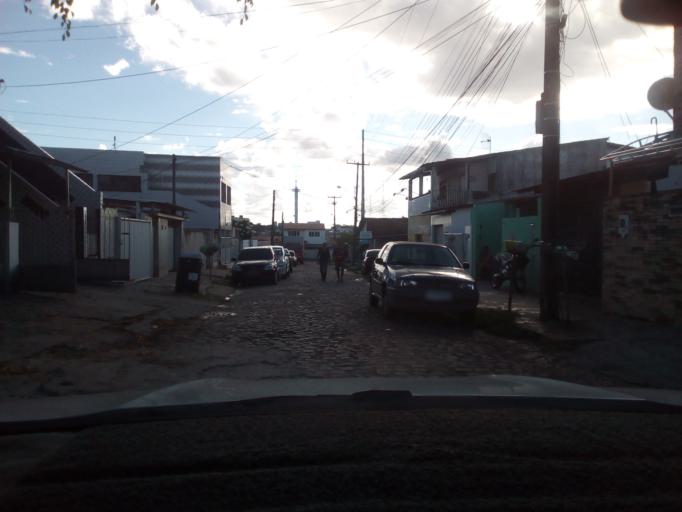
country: BR
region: Paraiba
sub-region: Joao Pessoa
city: Joao Pessoa
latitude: -7.1135
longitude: -34.8661
